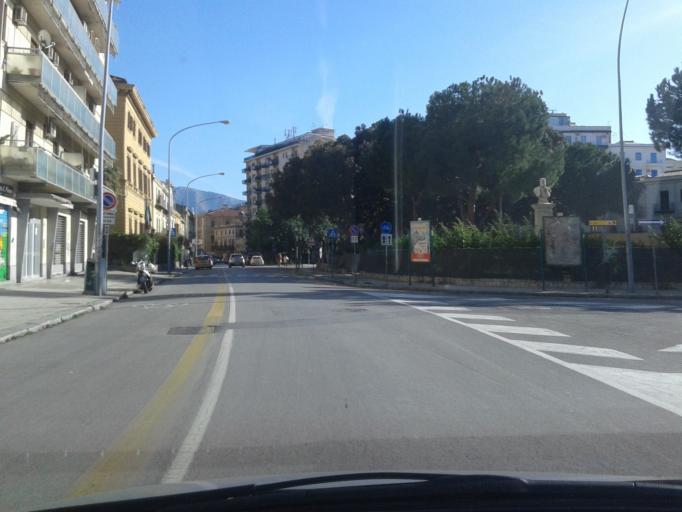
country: IT
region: Sicily
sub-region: Palermo
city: Palermo
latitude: 38.1204
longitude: 13.3409
